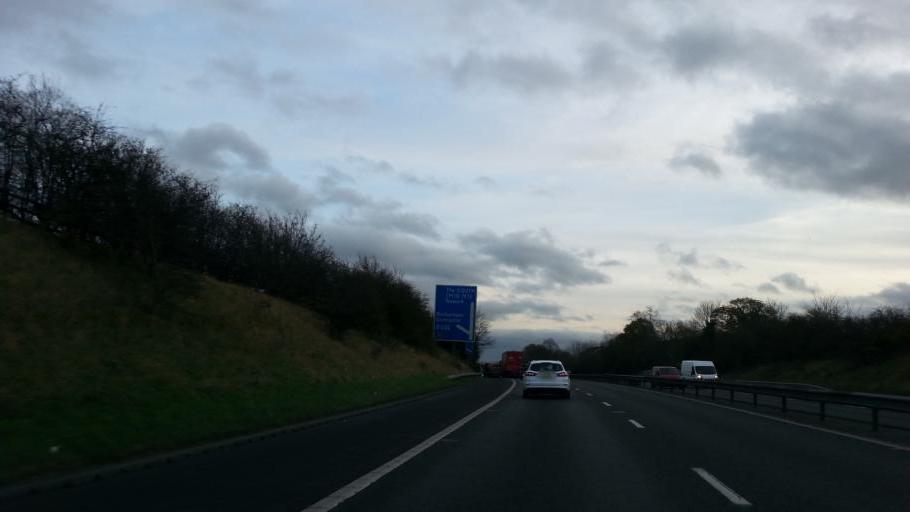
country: GB
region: England
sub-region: Doncaster
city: Bentley
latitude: 53.5052
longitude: -1.1771
